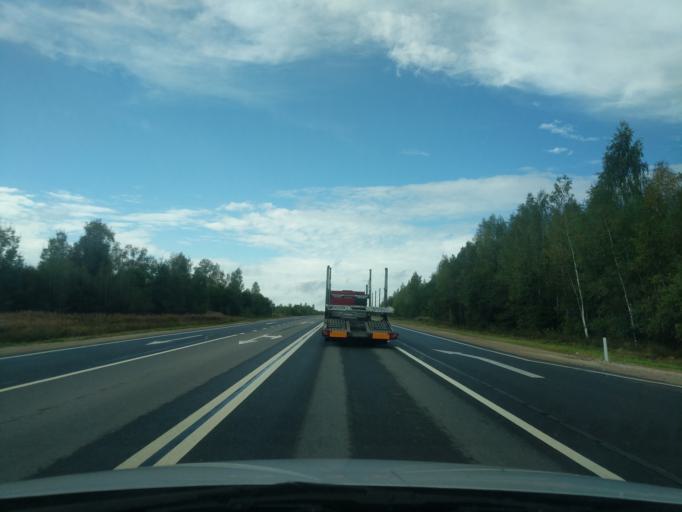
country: RU
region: Kostroma
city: Sudislavl'
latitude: 57.8176
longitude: 41.9440
